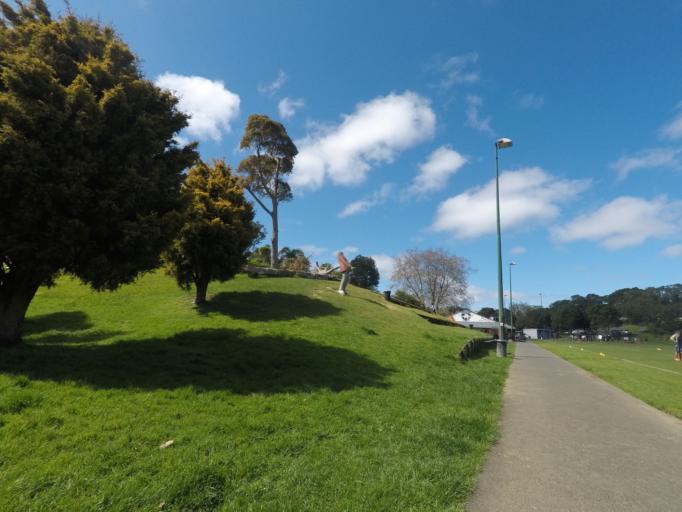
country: NZ
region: Auckland
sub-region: Auckland
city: Auckland
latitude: -36.8595
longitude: 174.7390
